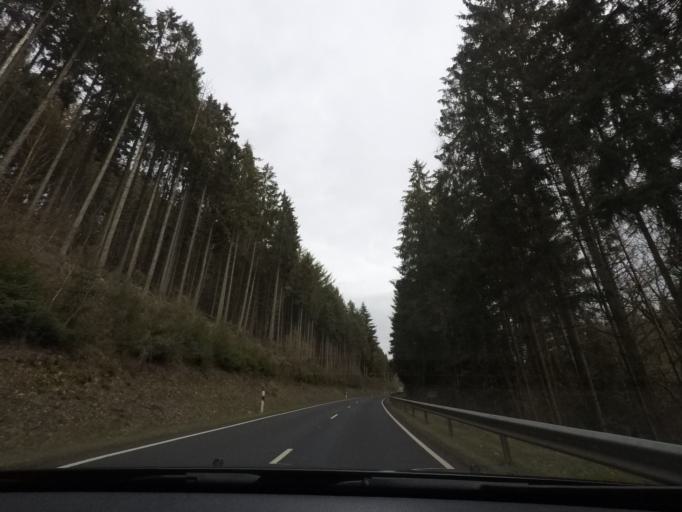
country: LU
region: Diekirch
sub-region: Canton de Wiltz
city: Winseler
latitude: 49.9969
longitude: 5.8596
